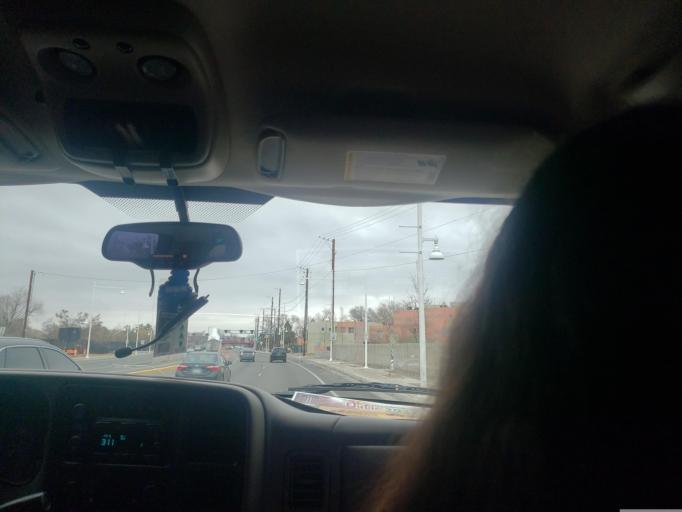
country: US
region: New Mexico
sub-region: Bernalillo County
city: Albuquerque
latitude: 35.0915
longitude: -106.6786
